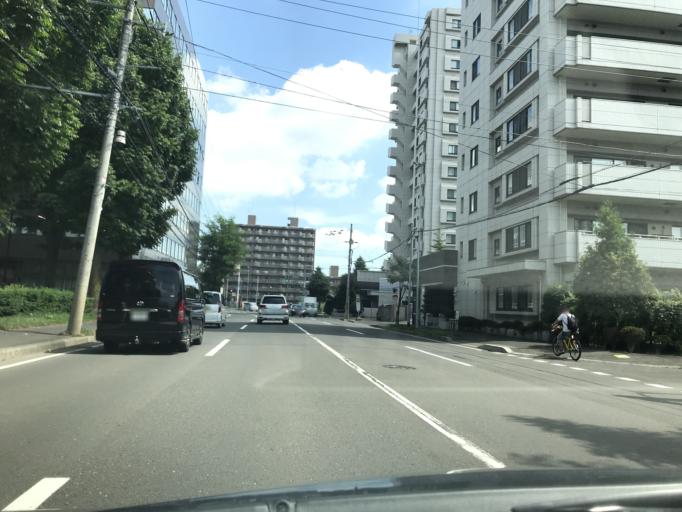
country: JP
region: Hokkaido
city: Sapporo
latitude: 43.0587
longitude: 141.3799
